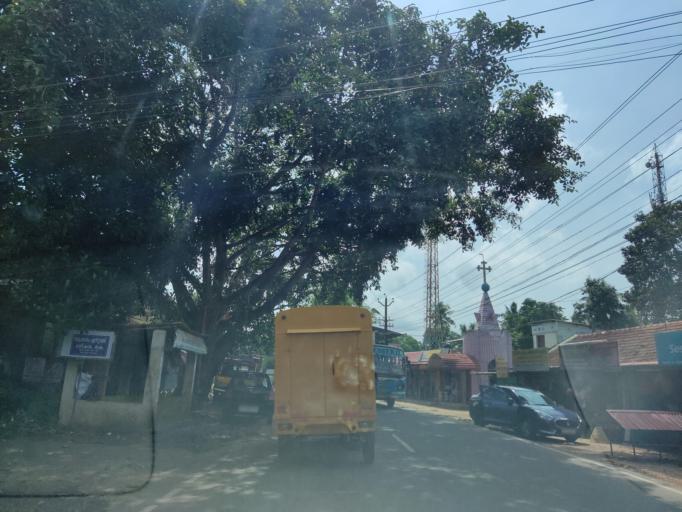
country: IN
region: Kerala
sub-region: Alappuzha
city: Mavelikara
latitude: 9.2789
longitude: 76.5331
